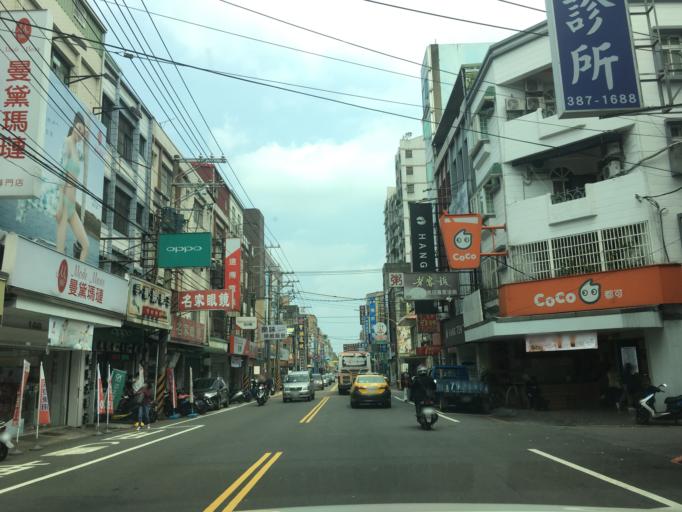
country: TW
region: Taiwan
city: Daxi
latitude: 24.8811
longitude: 121.2888
